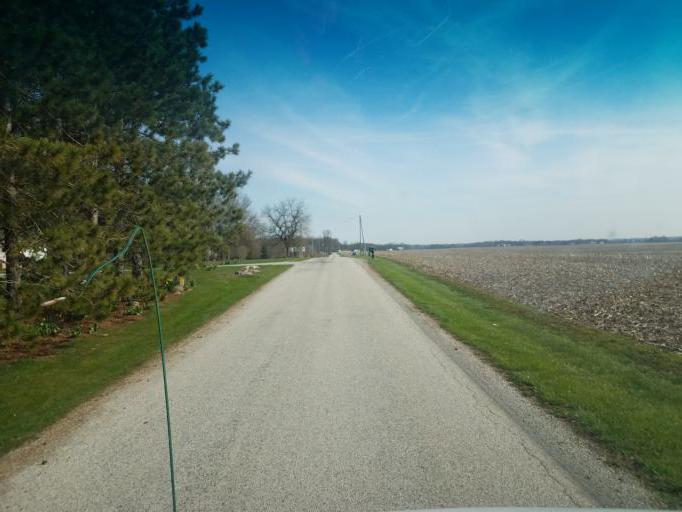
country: US
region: Ohio
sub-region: Richland County
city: Shelby
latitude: 40.8859
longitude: -82.5714
